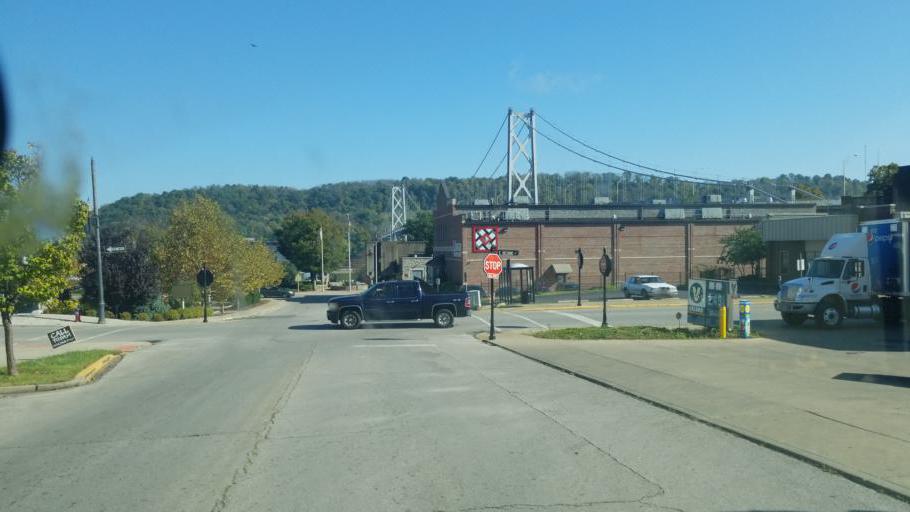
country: US
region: Ohio
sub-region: Brown County
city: Aberdeen
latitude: 38.6467
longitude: -83.7628
